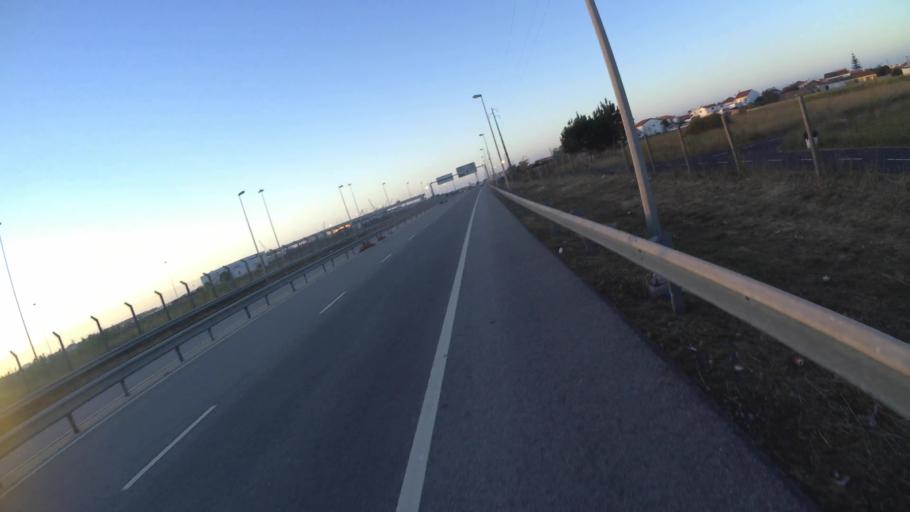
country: PT
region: Aveiro
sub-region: Ilhavo
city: Gafanha da Nazare
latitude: 40.6351
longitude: -8.7282
